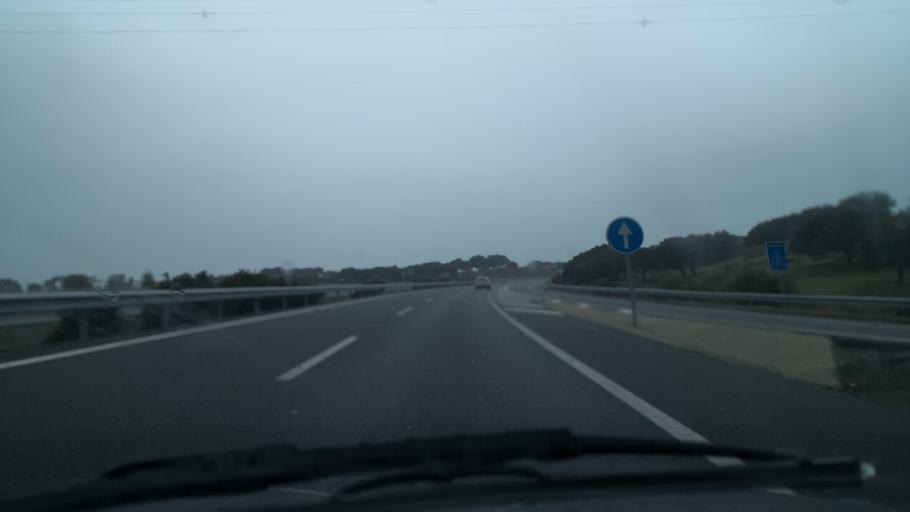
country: ES
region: Extremadura
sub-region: Provincia de Caceres
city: Plasencia
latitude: 40.0333
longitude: -6.1214
